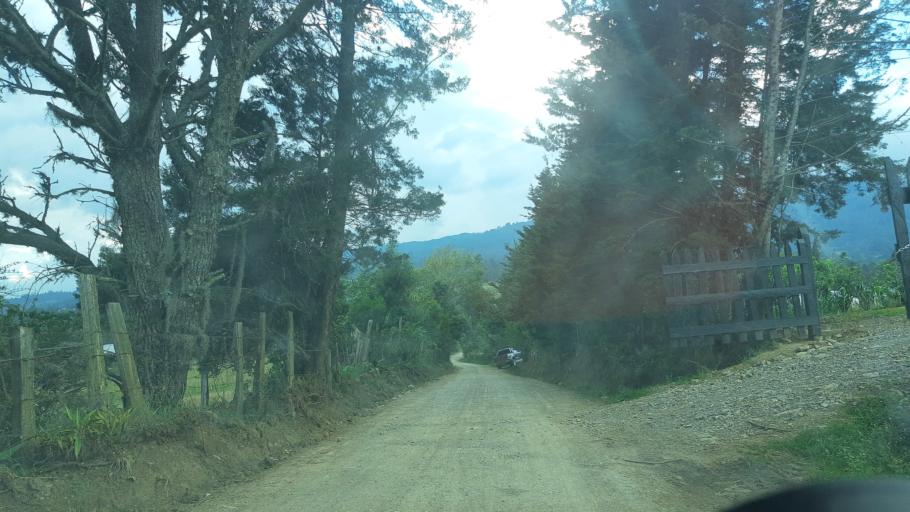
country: CO
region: Boyaca
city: Santa Sofia
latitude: 5.7312
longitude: -73.5974
